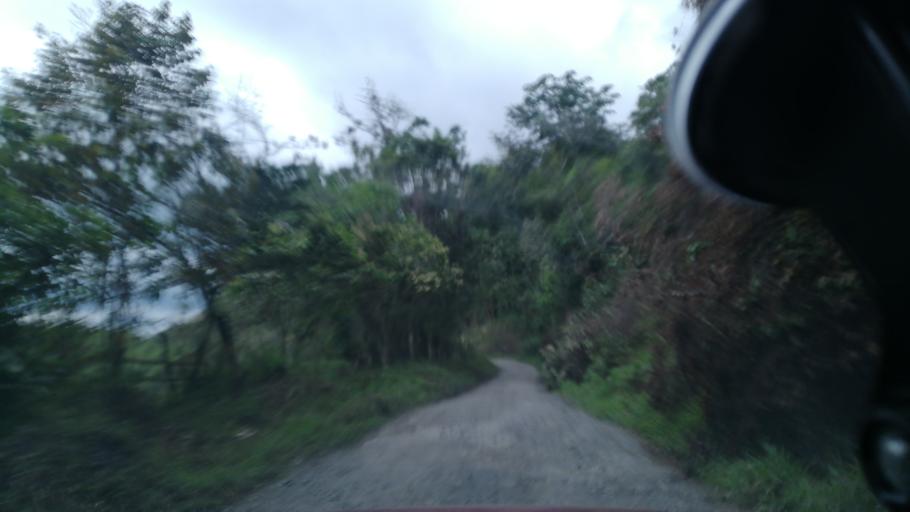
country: CO
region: Cundinamarca
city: Pacho
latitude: 5.1561
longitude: -74.2467
